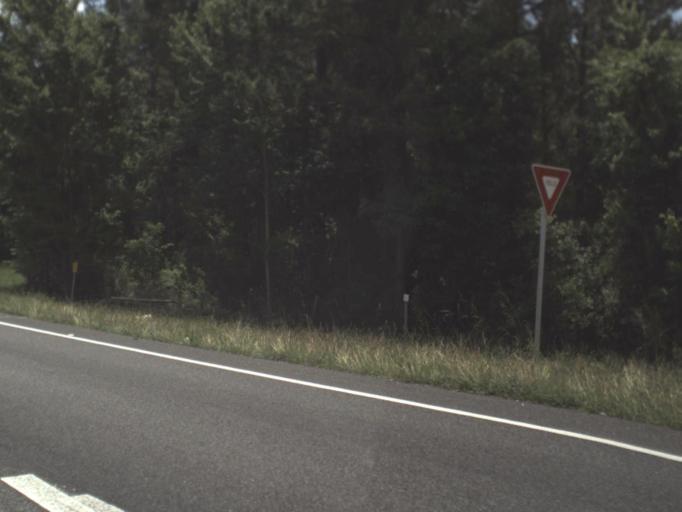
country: US
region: Florida
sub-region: Duval County
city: Jacksonville
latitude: 30.4563
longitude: -81.6303
